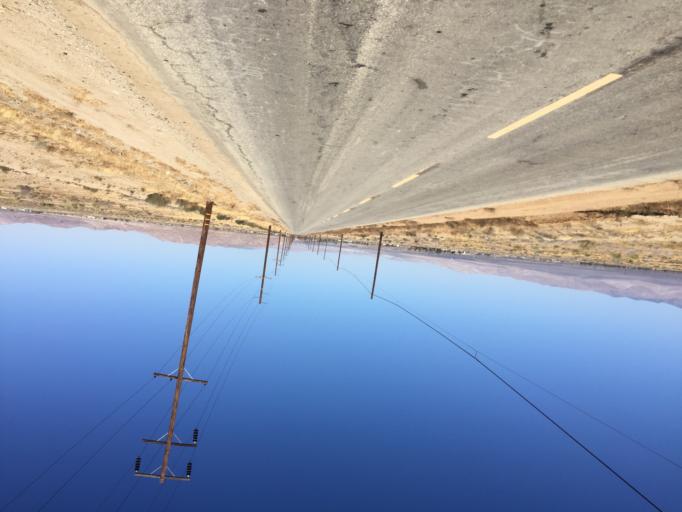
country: US
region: California
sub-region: Kern County
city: Rosamond
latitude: 34.8066
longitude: -118.2904
